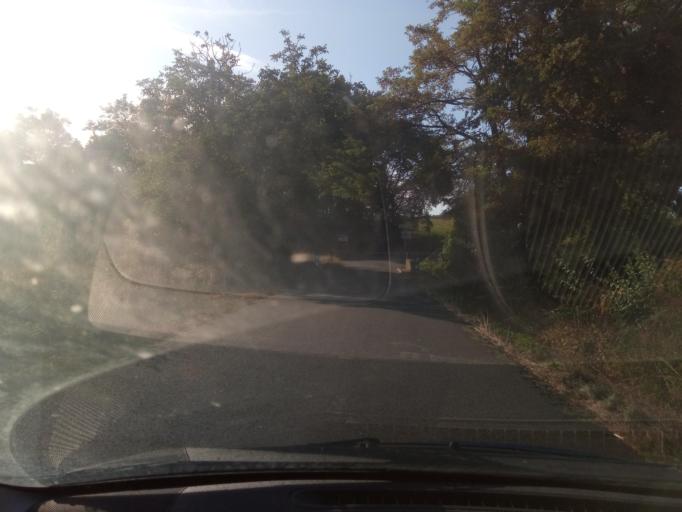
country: FR
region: Poitou-Charentes
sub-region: Departement de la Vienne
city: Montmorillon
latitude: 46.4965
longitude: 0.8305
